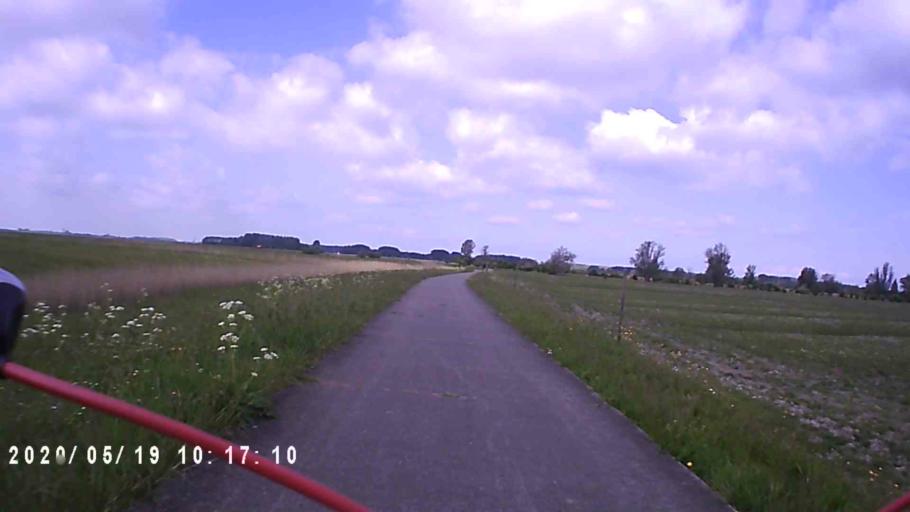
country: NL
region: Friesland
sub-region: Gemeente Kollumerland en Nieuwkruisland
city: Kollum
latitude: 53.3220
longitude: 6.2107
